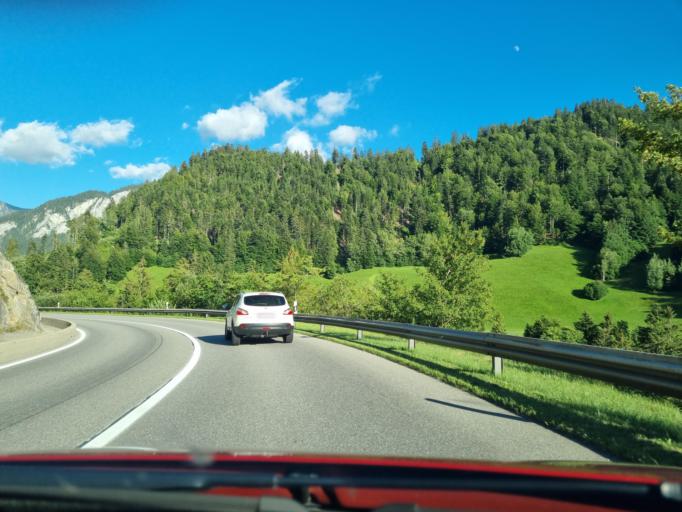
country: CH
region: Vaud
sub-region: Riviera-Pays-d'Enhaut District
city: Chateau-d'Oex
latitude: 46.4646
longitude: 7.0904
